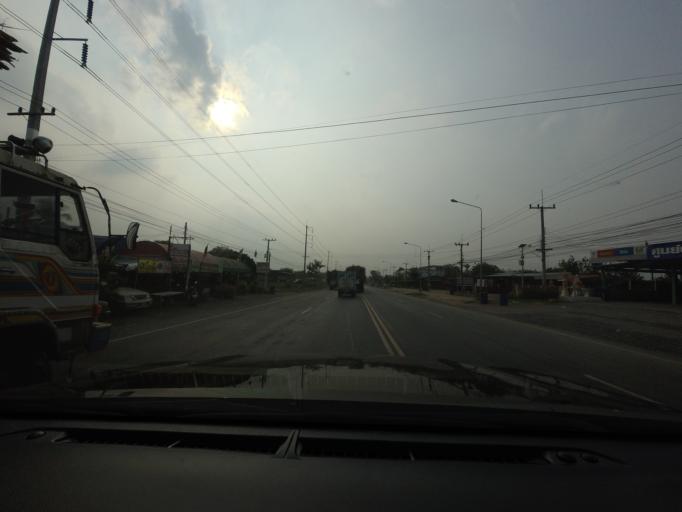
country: TH
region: Sara Buri
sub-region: Amphoe Wang Muang
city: Wang Muang
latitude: 14.8426
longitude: 101.1098
